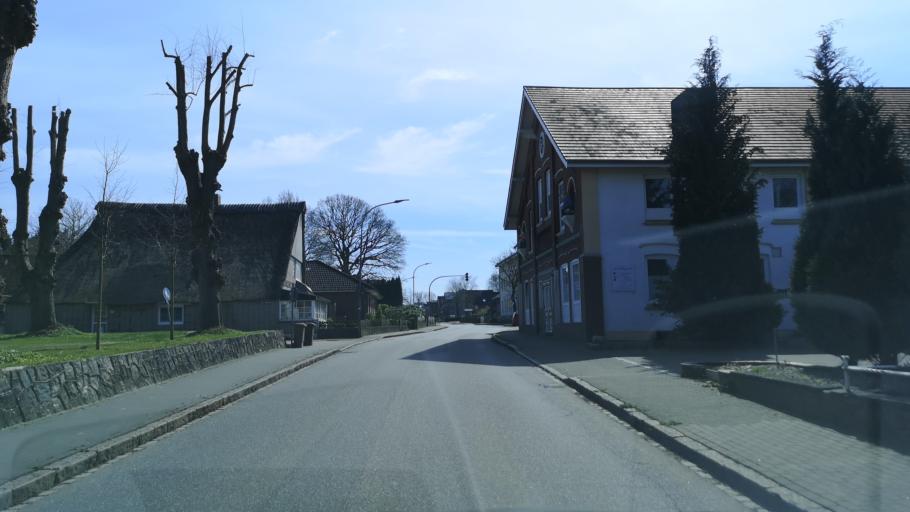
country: DE
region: Schleswig-Holstein
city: Munsterdorf
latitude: 53.9034
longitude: 9.5410
